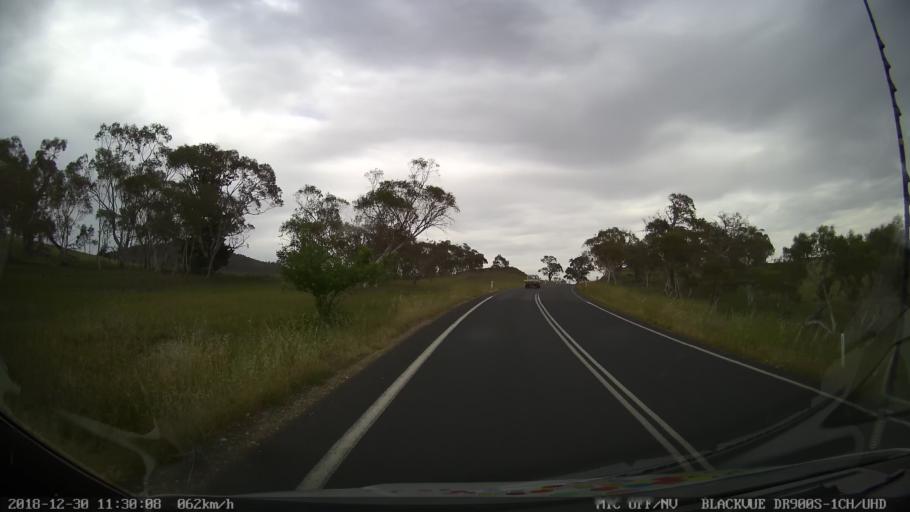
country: AU
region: New South Wales
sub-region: Snowy River
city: Jindabyne
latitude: -36.4452
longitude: 148.6065
